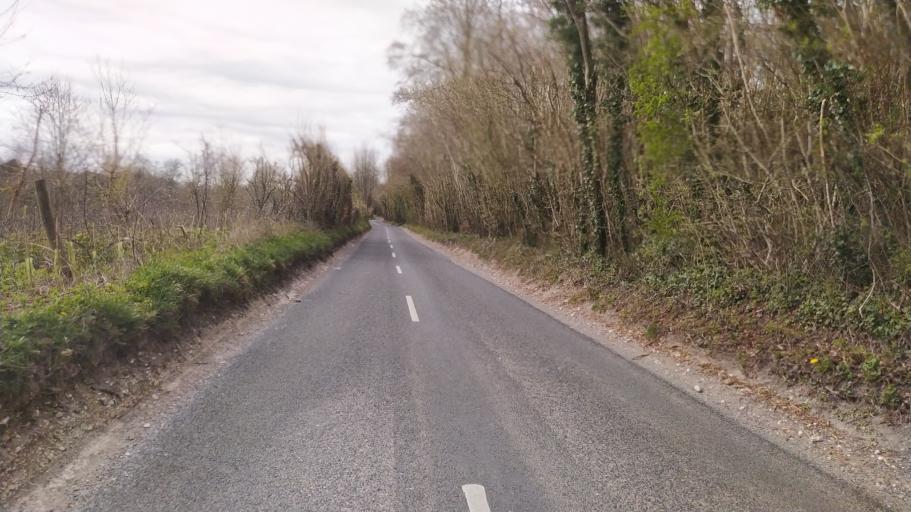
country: GB
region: England
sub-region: Hampshire
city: Bishops Waltham
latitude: 51.0089
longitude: -1.1952
